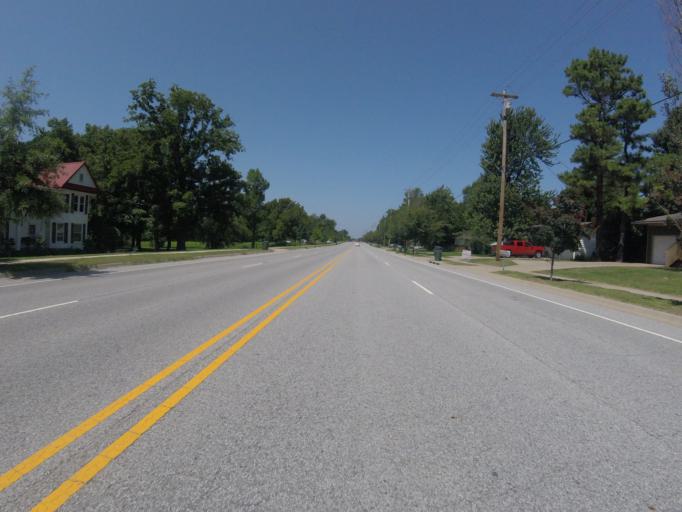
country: US
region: Arkansas
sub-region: Washington County
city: Fayetteville
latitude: 36.0927
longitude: -94.2001
